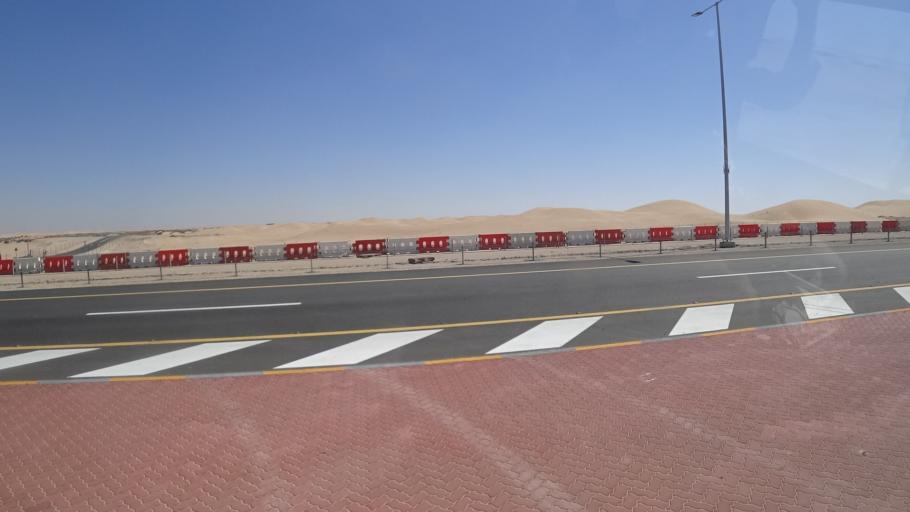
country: AE
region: Abu Dhabi
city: Abu Dhabi
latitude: 24.1216
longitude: 54.8347
